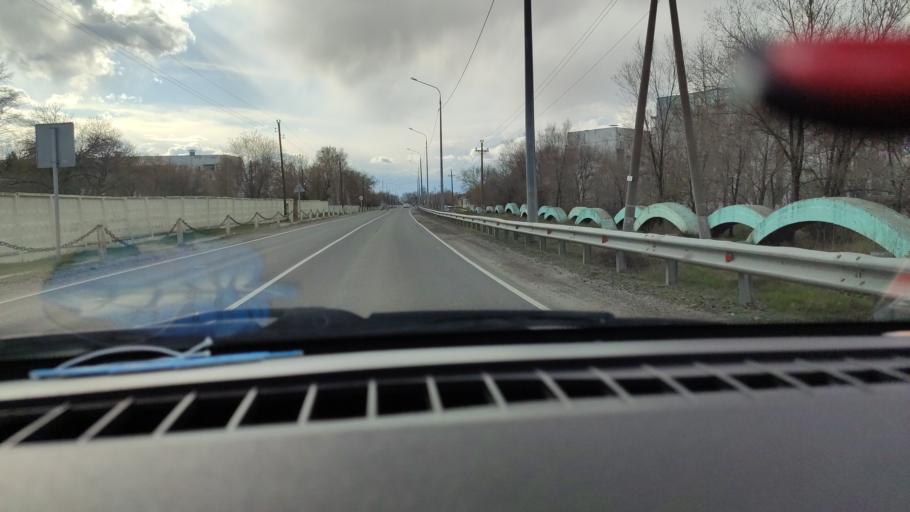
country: RU
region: Saratov
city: Sennoy
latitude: 52.1531
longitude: 46.9535
